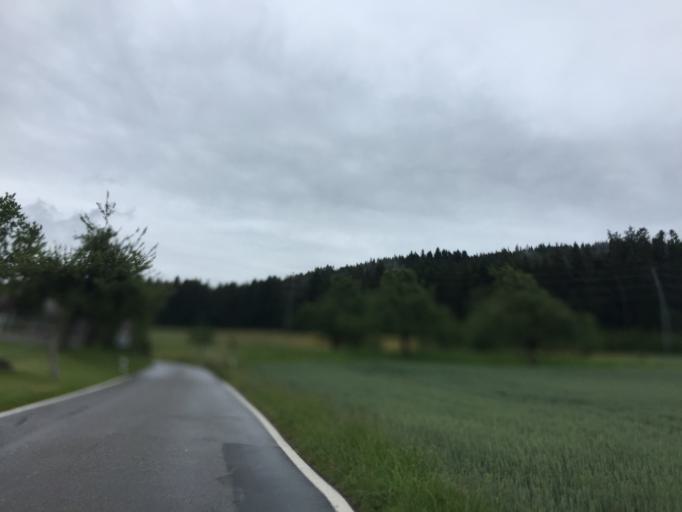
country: CH
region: Bern
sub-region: Bern-Mittelland District
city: Biglen
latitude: 46.9062
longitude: 7.6153
